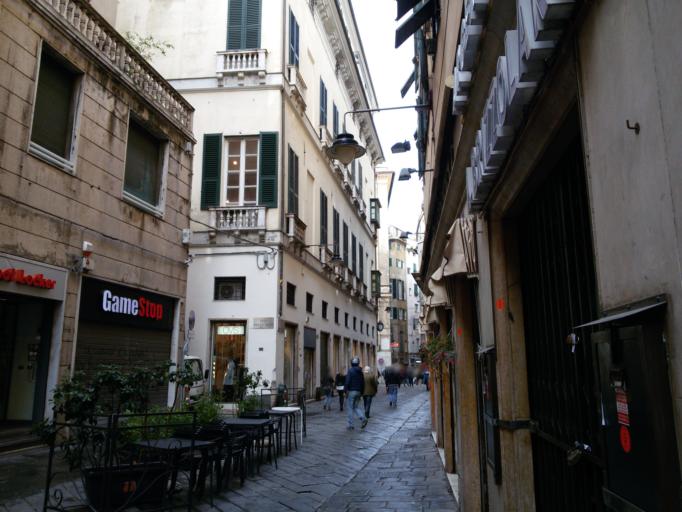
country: IT
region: Liguria
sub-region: Provincia di Genova
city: San Teodoro
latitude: 44.4095
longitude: 8.9321
